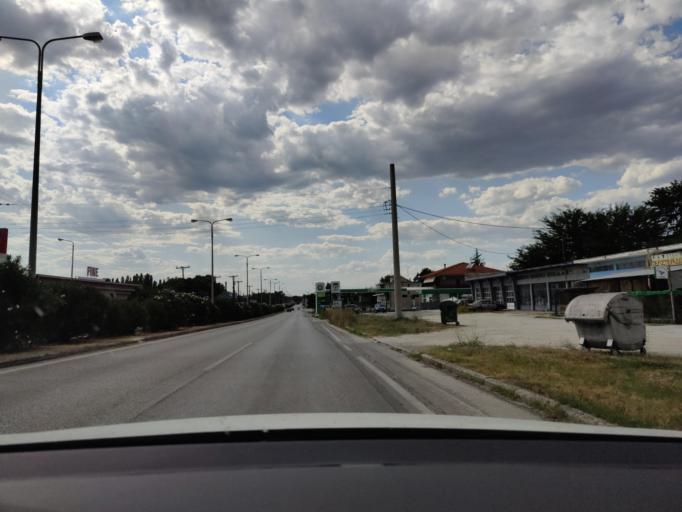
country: GR
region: Central Macedonia
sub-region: Nomos Serron
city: Lefkonas
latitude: 41.0904
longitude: 23.5178
